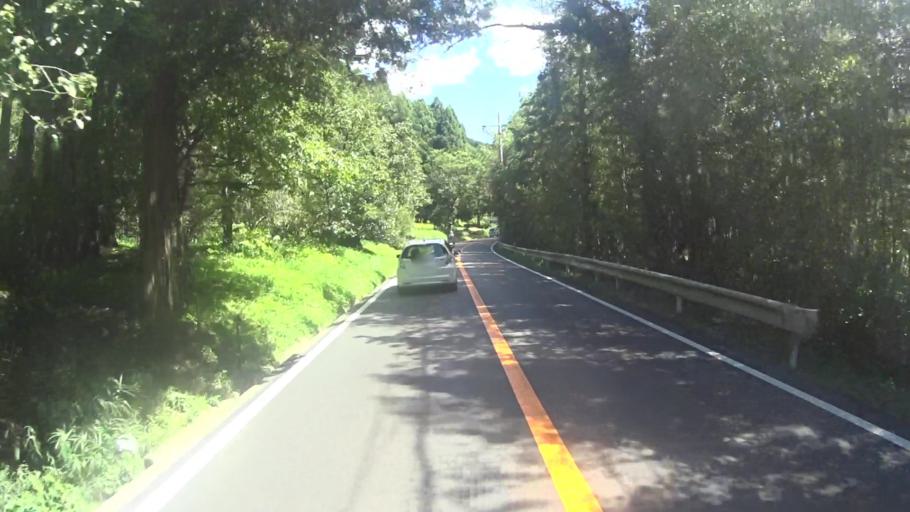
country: JP
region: Nara
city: Nara-shi
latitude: 34.7647
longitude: 135.9210
